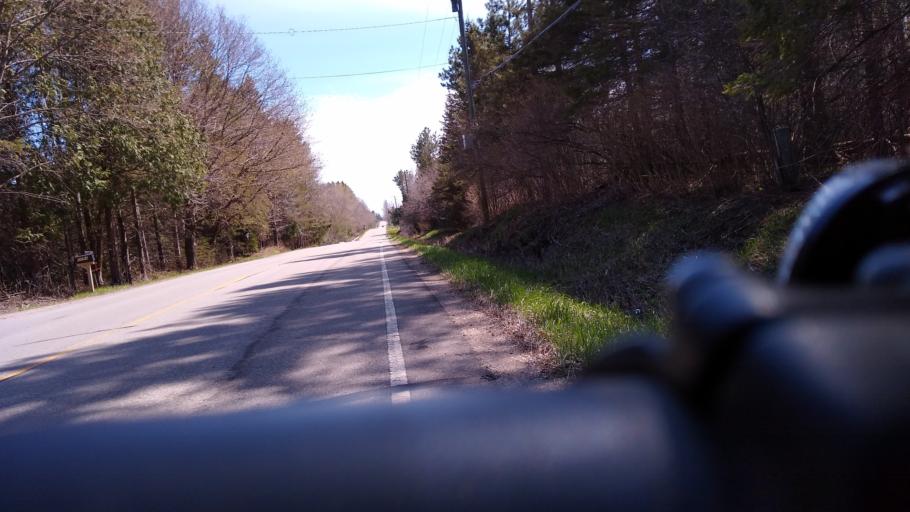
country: US
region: Michigan
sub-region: Delta County
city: Escanaba
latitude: 45.7307
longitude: -87.2025
